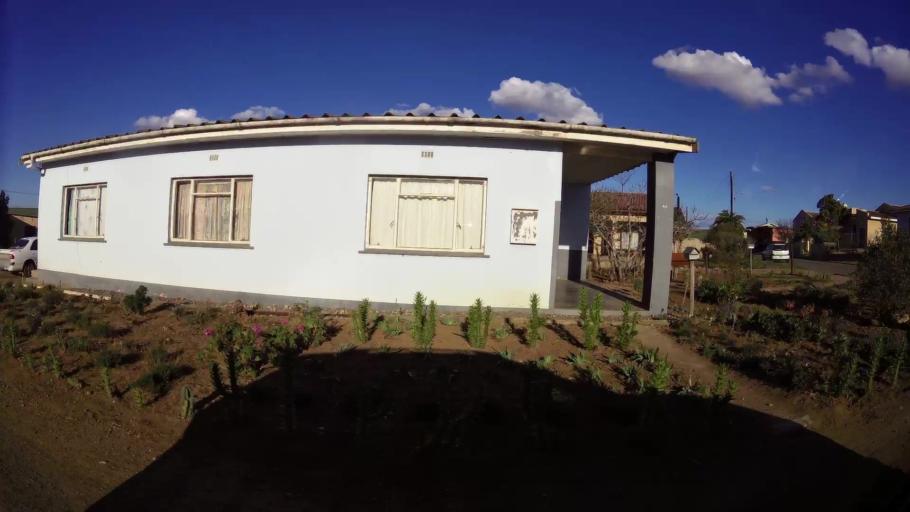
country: ZA
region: Western Cape
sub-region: Eden District Municipality
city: Riversdale
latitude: -34.1041
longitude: 20.9599
